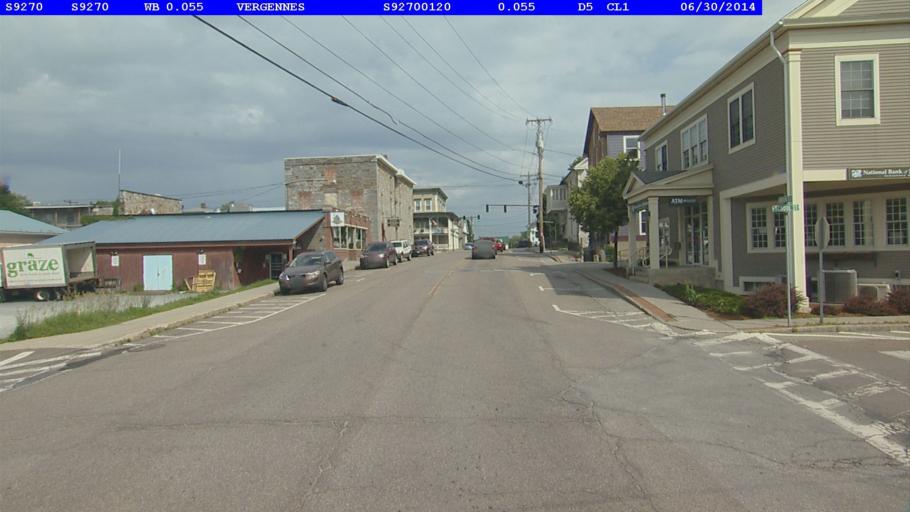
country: US
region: Vermont
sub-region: Addison County
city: Vergennes
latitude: 44.1672
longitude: -73.2513
